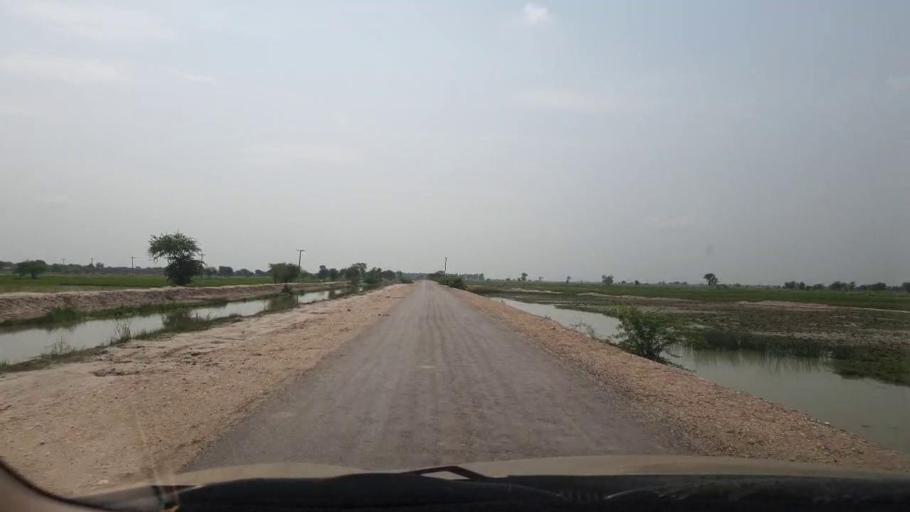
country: PK
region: Sindh
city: Goth Garelo
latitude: 27.5164
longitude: 68.1045
